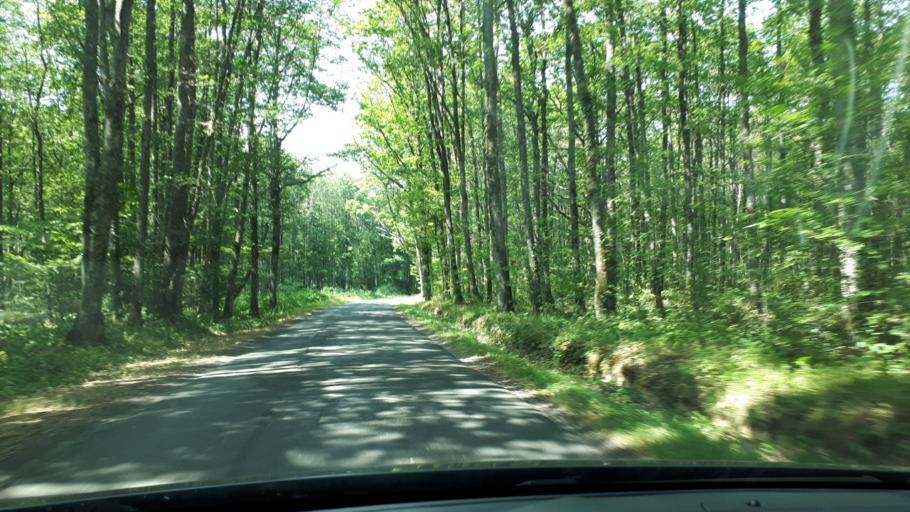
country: FR
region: Centre
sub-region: Departement du Loir-et-Cher
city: Naveil
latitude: 47.8324
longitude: 1.0350
